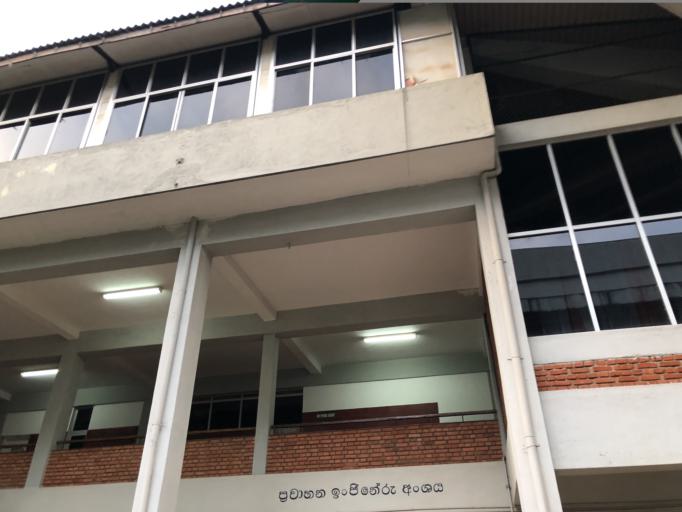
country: LK
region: Western
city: Moratuwa
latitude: 6.7982
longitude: 79.9027
